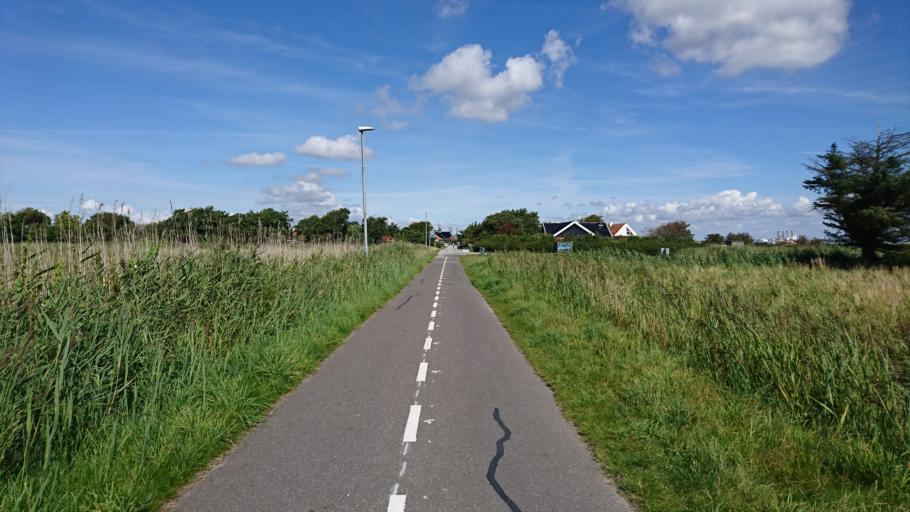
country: DK
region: South Denmark
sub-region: Fano Kommune
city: Nordby
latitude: 55.4354
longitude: 8.3955
